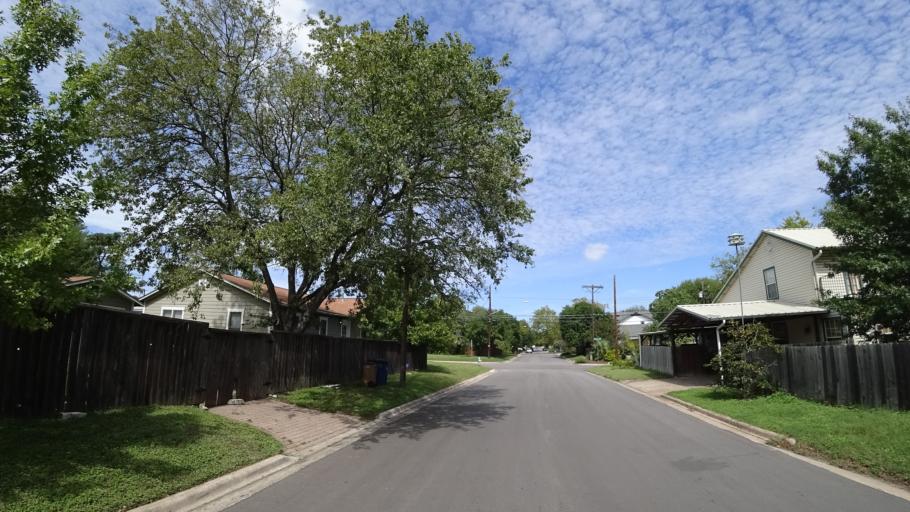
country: US
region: Texas
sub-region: Travis County
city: Austin
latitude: 30.3391
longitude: -97.7378
